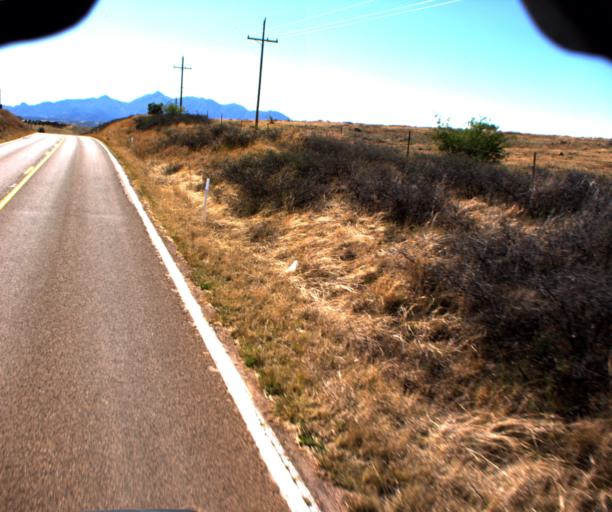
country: US
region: Arizona
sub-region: Cochise County
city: Huachuca City
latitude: 31.6737
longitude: -110.6284
